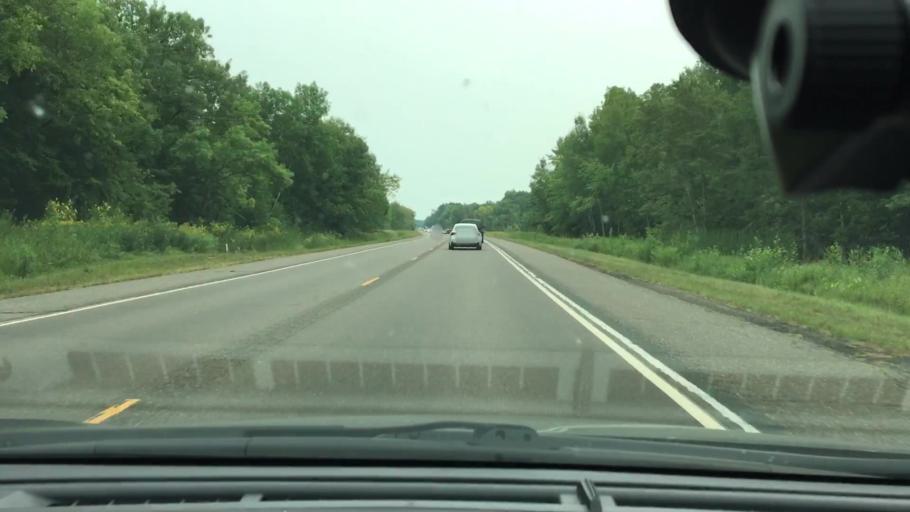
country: US
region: Minnesota
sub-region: Mille Lacs County
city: Vineland
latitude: 46.1501
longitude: -93.7403
